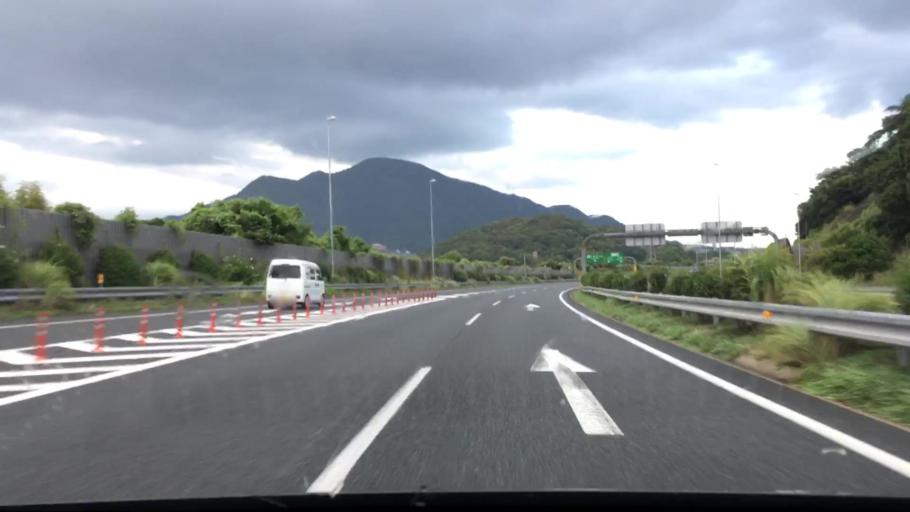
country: JP
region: Fukuoka
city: Kitakyushu
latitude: 33.8217
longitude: 130.8877
